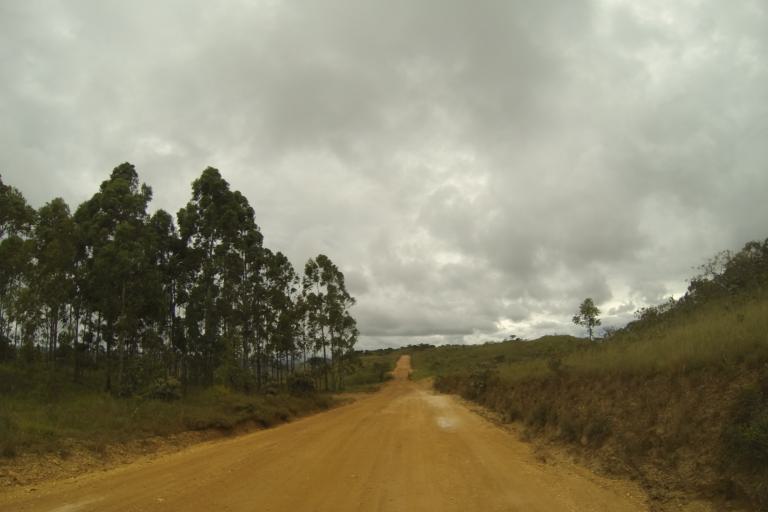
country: BR
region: Minas Gerais
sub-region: Ibia
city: Ibia
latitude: -19.7427
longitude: -46.4594
